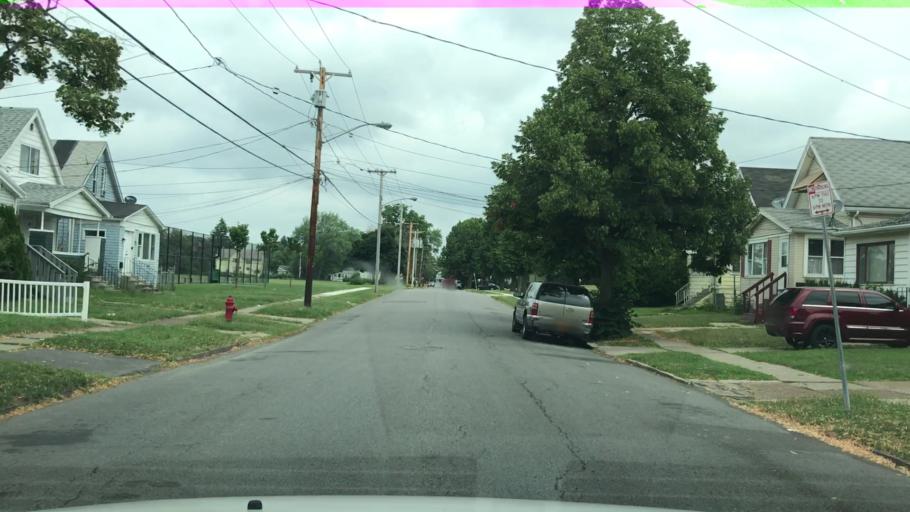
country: US
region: New York
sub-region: Erie County
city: Sloan
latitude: 42.9110
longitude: -78.8038
